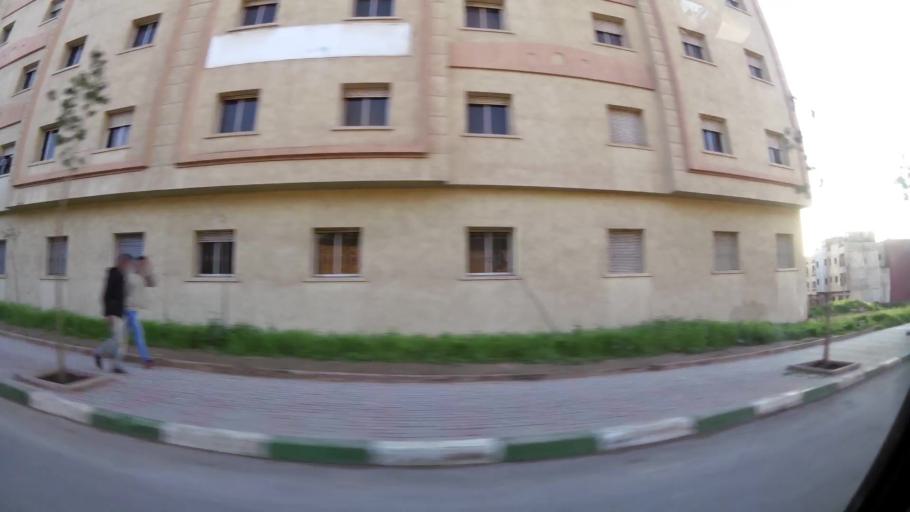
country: MA
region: Chaouia-Ouardigha
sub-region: Settat Province
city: Settat
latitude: 32.9935
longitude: -7.6144
